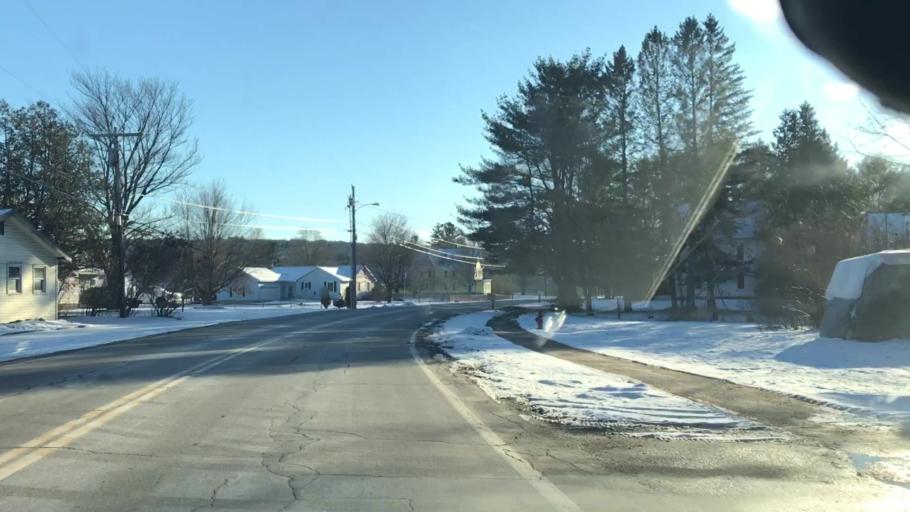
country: US
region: New Hampshire
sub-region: Grafton County
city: North Haverhill
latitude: 44.0847
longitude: -72.0252
